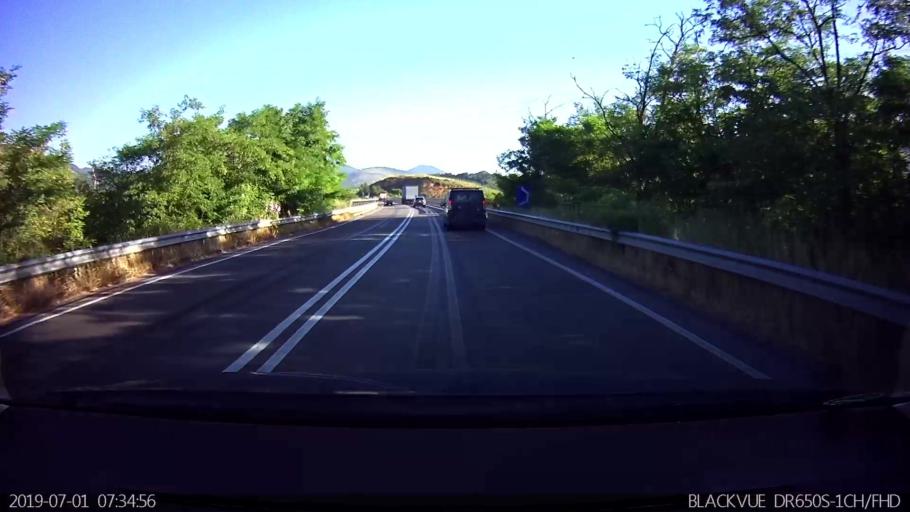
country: IT
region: Latium
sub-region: Provincia di Latina
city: Prossedi
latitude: 41.5205
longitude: 13.2727
